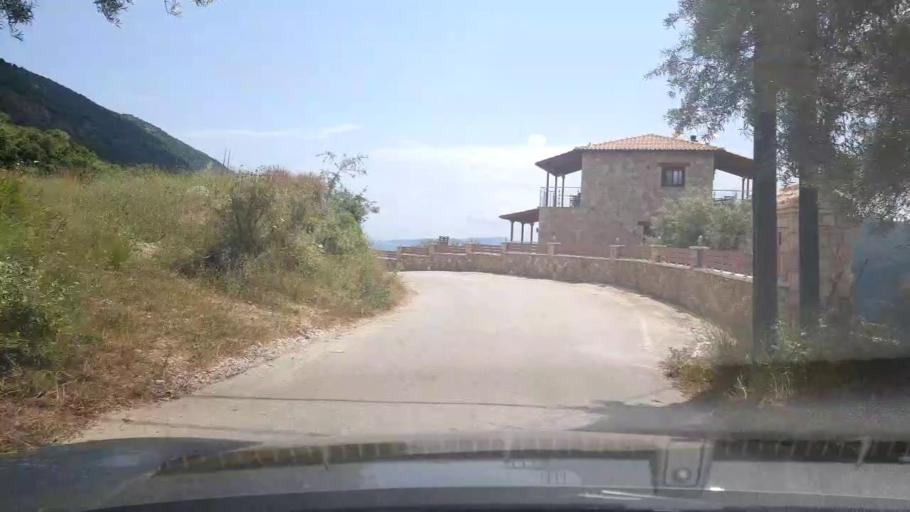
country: GR
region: Ionian Islands
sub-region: Lefkada
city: Nidri
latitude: 38.6444
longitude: 20.6993
